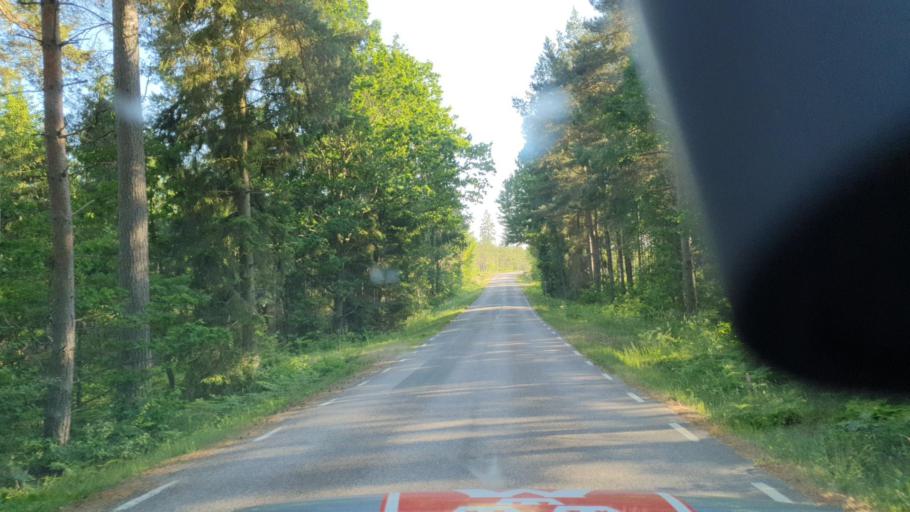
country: SE
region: Kalmar
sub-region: Torsas Kommun
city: Torsas
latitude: 56.4918
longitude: 16.1015
